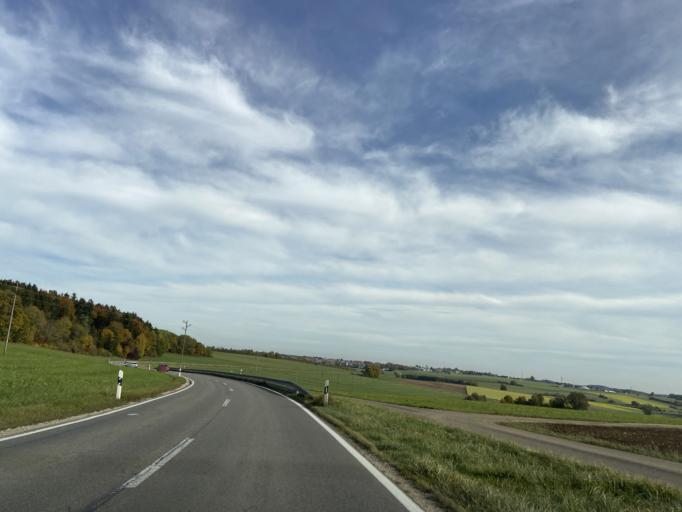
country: DE
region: Baden-Wuerttemberg
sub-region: Tuebingen Region
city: Stetten am Kalten Markt
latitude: 48.1187
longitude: 9.0453
